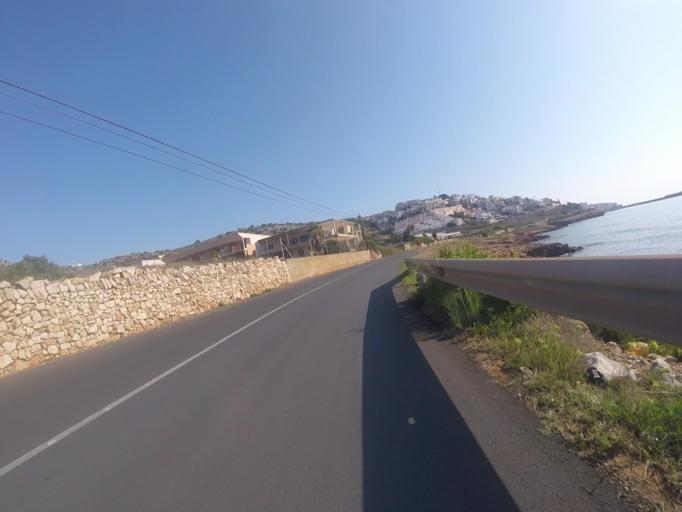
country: ES
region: Valencia
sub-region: Provincia de Castello
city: Peniscola
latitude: 40.3515
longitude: 0.3919
